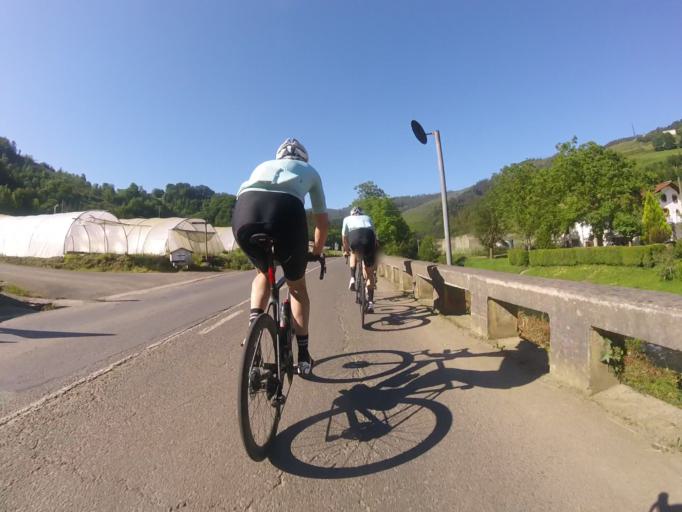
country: ES
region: Basque Country
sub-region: Provincia de Guipuzcoa
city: Beizama
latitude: 43.1461
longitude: -2.2322
